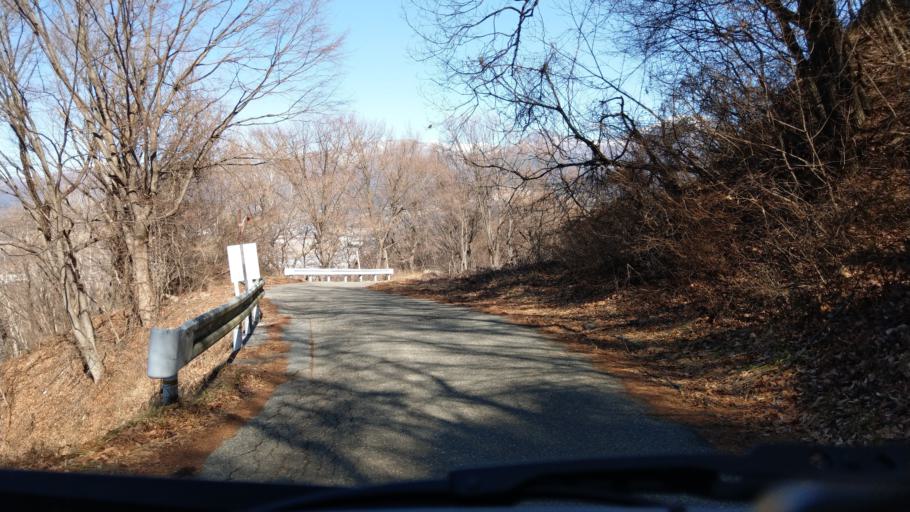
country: JP
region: Nagano
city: Komoro
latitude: 36.3166
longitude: 138.4045
